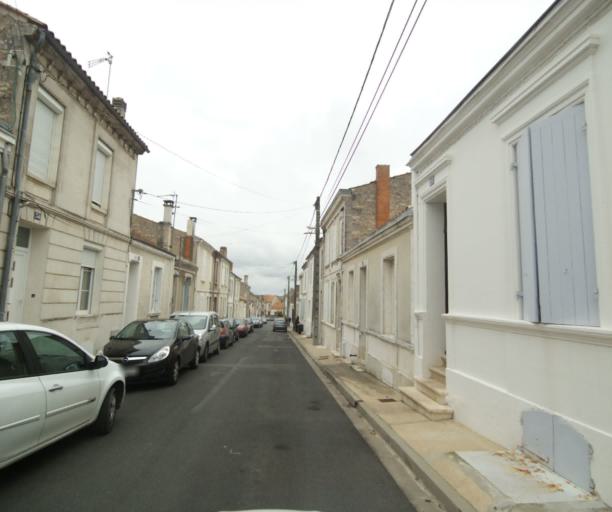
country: FR
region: Poitou-Charentes
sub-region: Departement de la Charente-Maritime
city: Saintes
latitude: 45.7467
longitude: -0.6116
